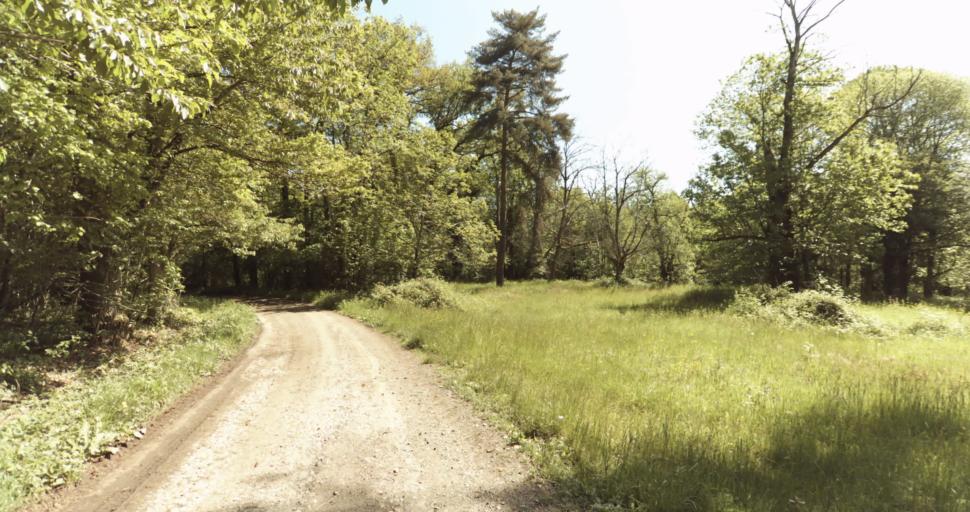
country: FR
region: Limousin
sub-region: Departement de la Haute-Vienne
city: Le Vigen
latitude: 45.7246
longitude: 1.3033
